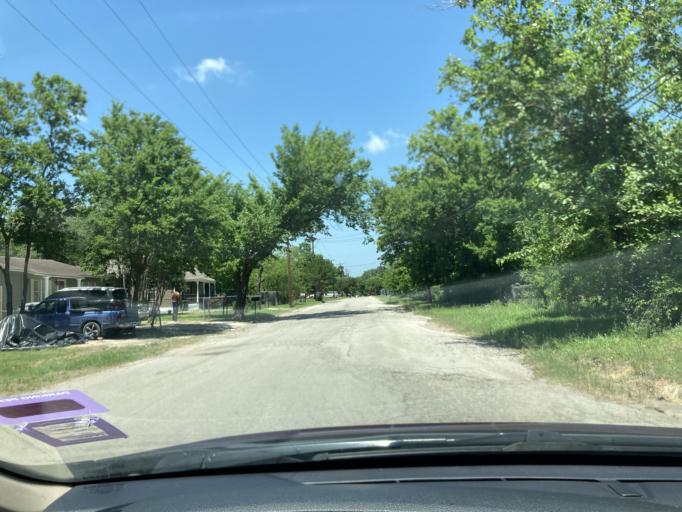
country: US
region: Texas
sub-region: Navarro County
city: Corsicana
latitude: 32.0800
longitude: -96.4644
